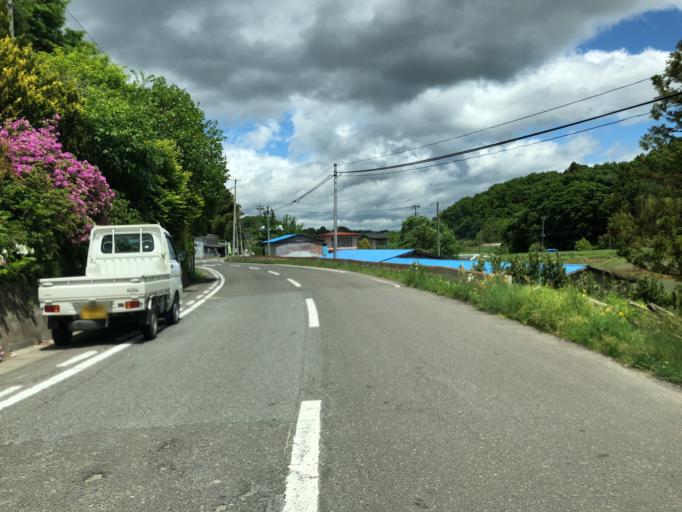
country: JP
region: Fukushima
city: Nihommatsu
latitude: 37.5481
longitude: 140.4691
